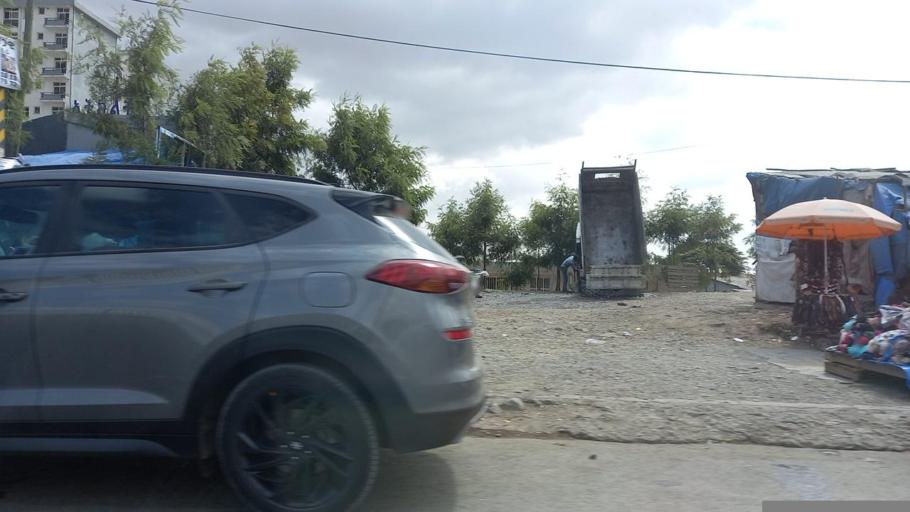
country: ET
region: Adis Abeba
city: Addis Ababa
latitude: 9.0208
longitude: 38.8653
